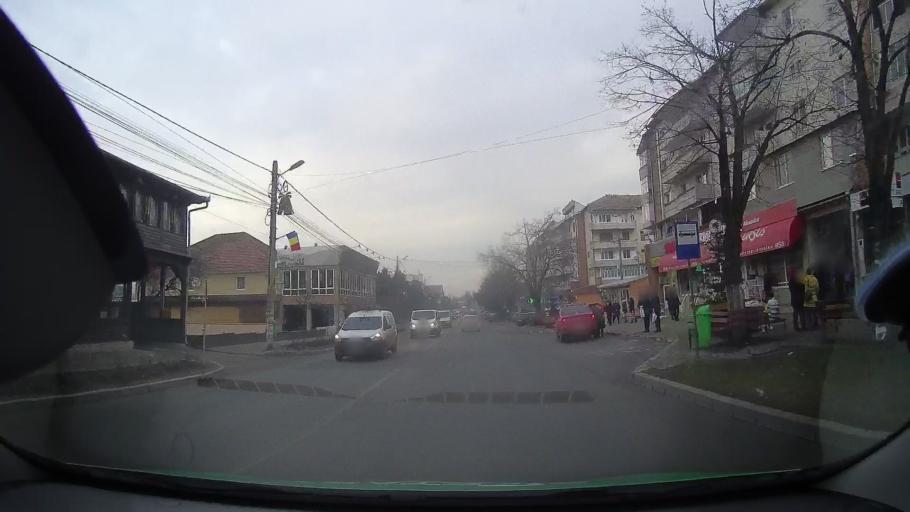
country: RO
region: Mures
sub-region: Comuna Ludus
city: Ludus
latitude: 46.4756
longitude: 24.0955
